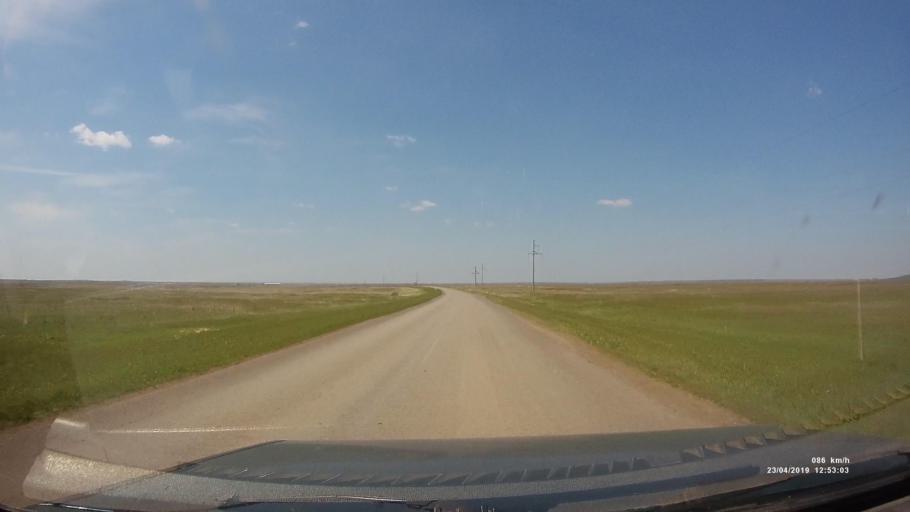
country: RU
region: Kalmykiya
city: Yashalta
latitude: 46.5706
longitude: 42.6014
